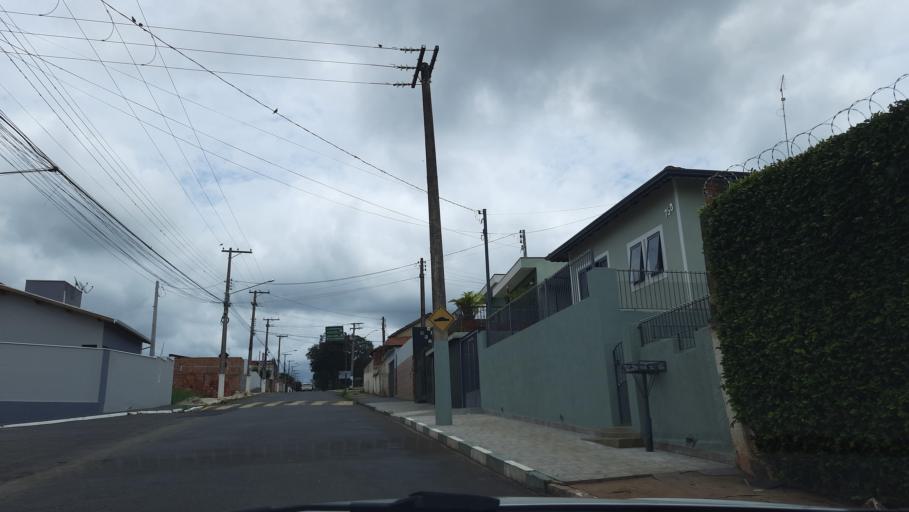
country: BR
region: Sao Paulo
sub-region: Casa Branca
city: Casa Branca
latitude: -21.7790
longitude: -47.0920
